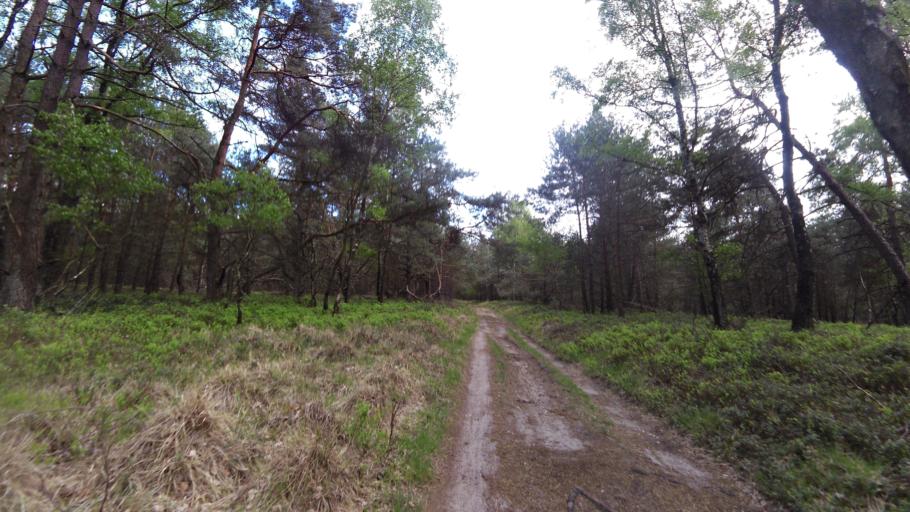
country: NL
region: Gelderland
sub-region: Gemeente Rozendaal
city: Rozendaal
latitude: 52.0482
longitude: 5.9431
